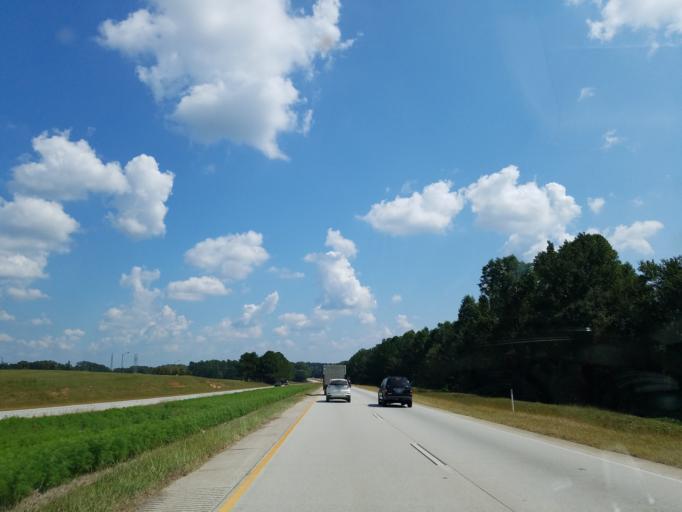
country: US
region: Georgia
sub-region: Barrow County
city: Russell
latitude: 33.9406
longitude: -83.7396
